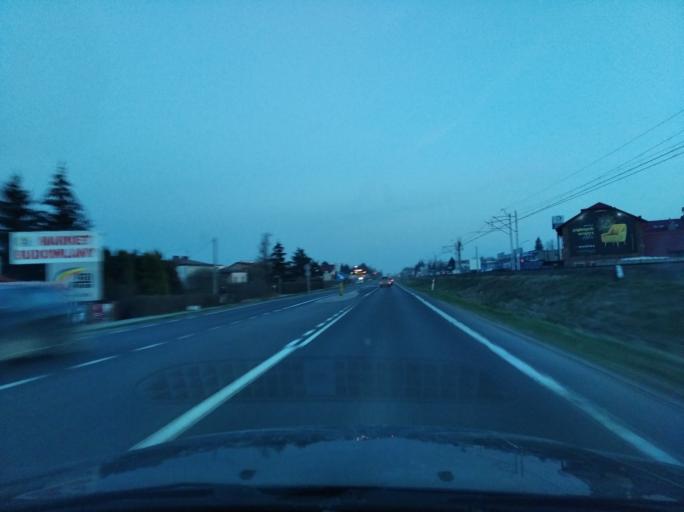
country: PL
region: Subcarpathian Voivodeship
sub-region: Powiat rzeszowski
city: Rudna Mala
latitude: 50.0858
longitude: 21.9837
